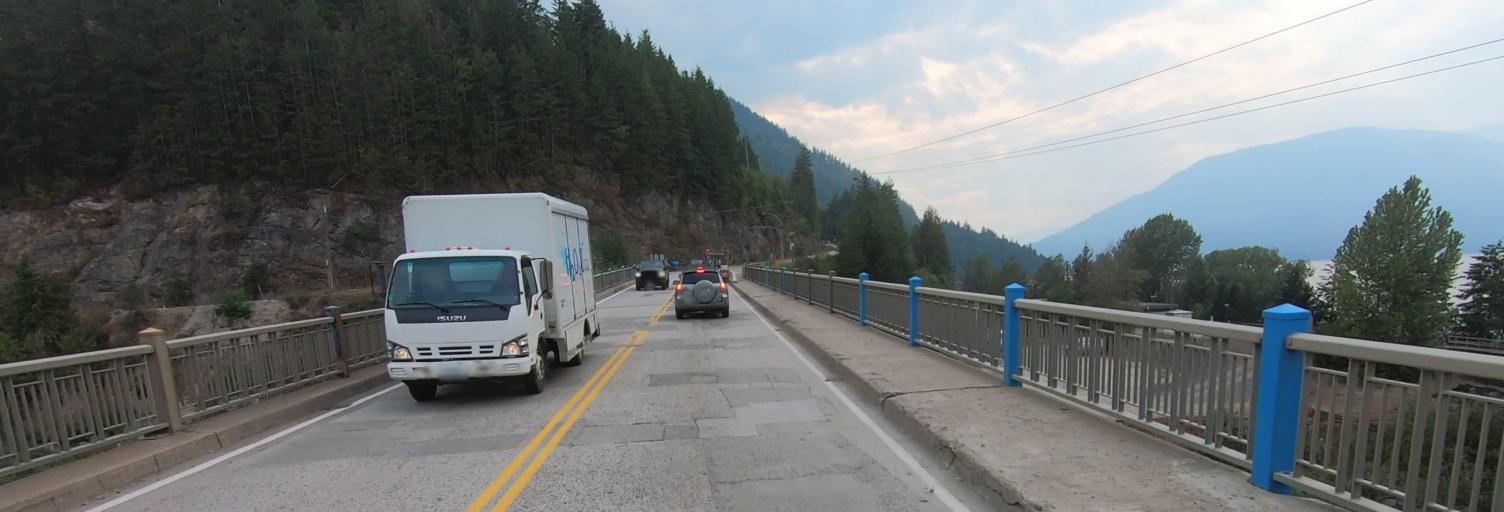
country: CA
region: British Columbia
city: Sicamous
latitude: 50.8360
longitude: -118.9940
